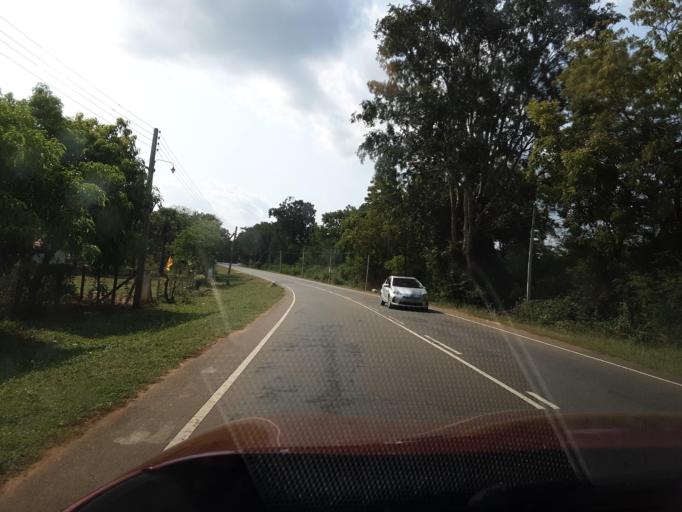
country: LK
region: Uva
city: Haputale
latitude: 6.3657
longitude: 81.1770
